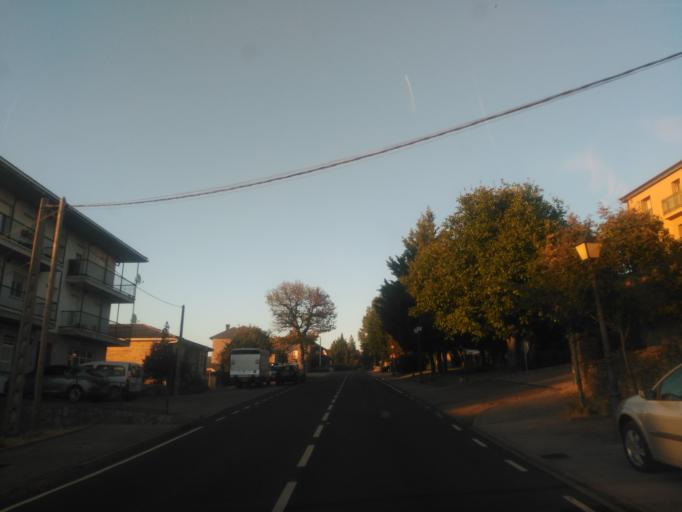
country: ES
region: Castille and Leon
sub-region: Provincia de Zamora
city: Puebla de Sanabria
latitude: 42.0561
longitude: -6.6292
